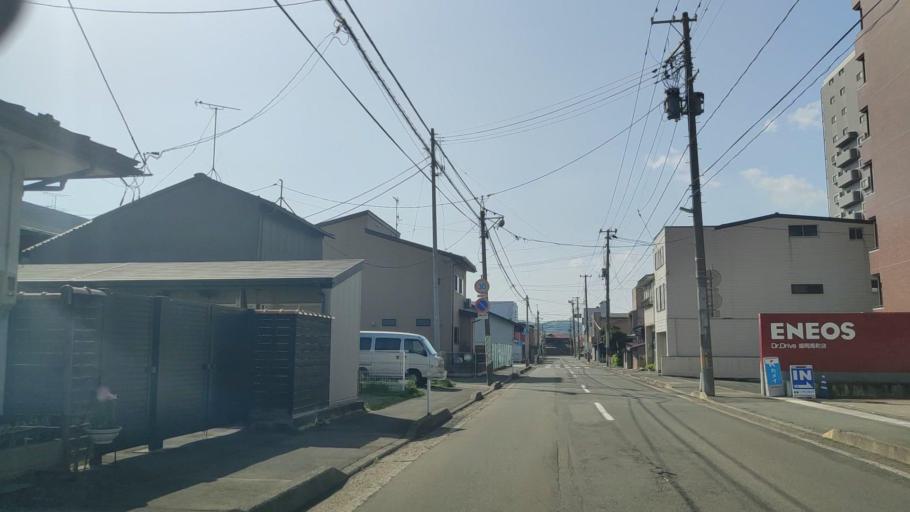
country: JP
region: Iwate
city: Morioka-shi
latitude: 39.6962
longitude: 141.1535
